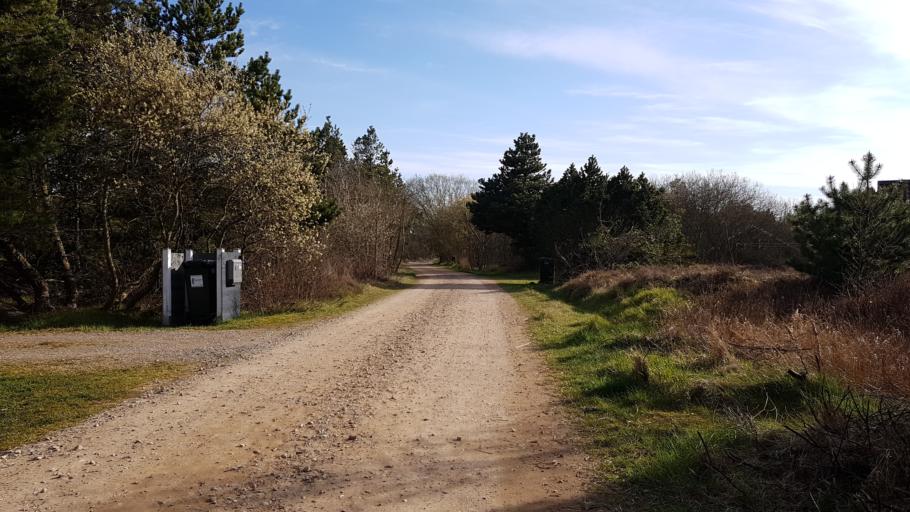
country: DE
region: Schleswig-Holstein
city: List
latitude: 55.1311
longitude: 8.5266
